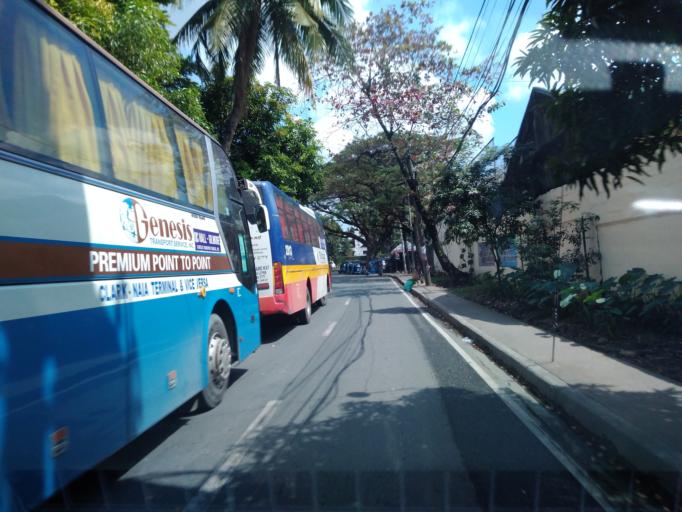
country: PH
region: Metro Manila
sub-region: Quezon City
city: Quezon City
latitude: 14.6502
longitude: 121.0532
